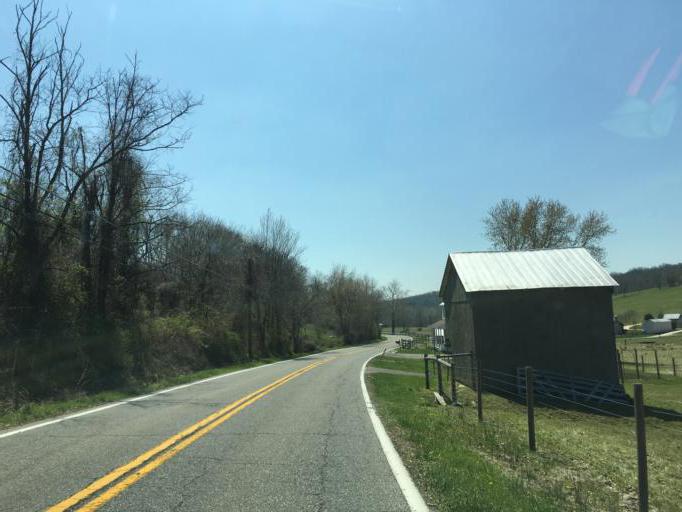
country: US
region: Maryland
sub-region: Frederick County
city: Myersville
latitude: 39.5582
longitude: -77.5248
